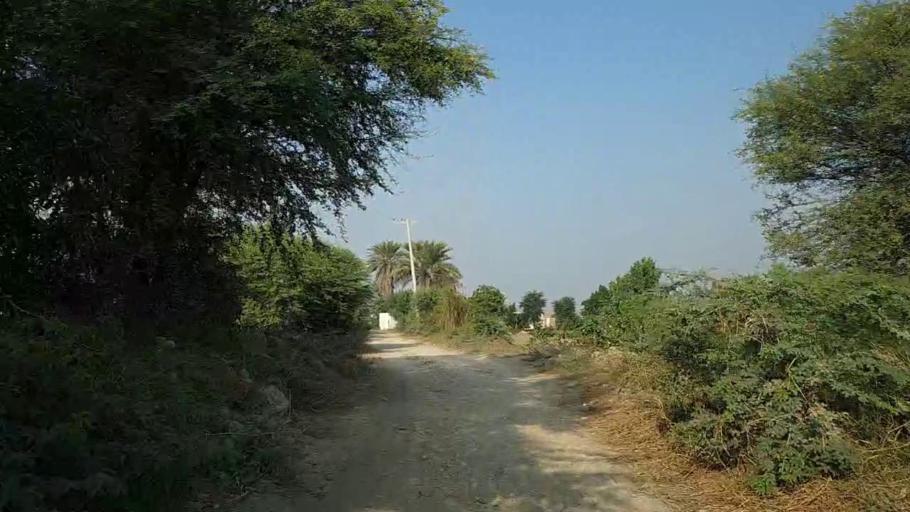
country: PK
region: Sindh
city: Mirpur Sakro
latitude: 24.6192
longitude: 67.7433
